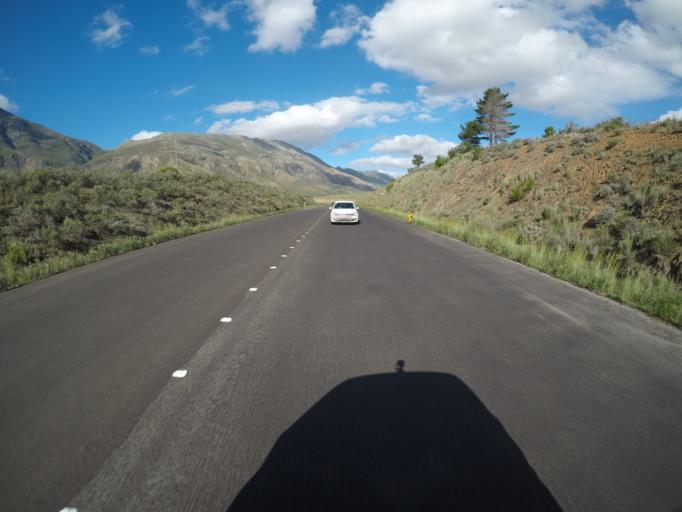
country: ZA
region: Western Cape
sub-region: Cape Winelands District Municipality
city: Ashton
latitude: -33.8725
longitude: 20.1495
